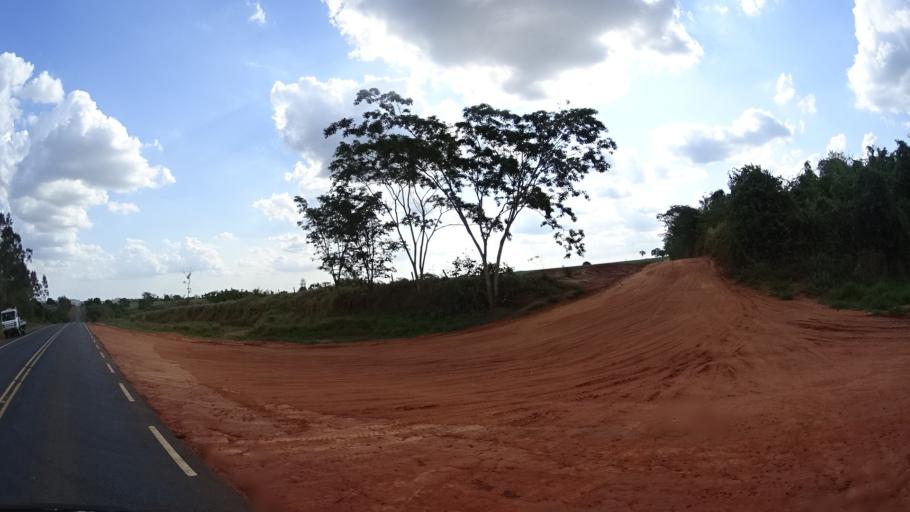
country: BR
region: Sao Paulo
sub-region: Urupes
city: Urupes
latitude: -21.1138
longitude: -49.2684
